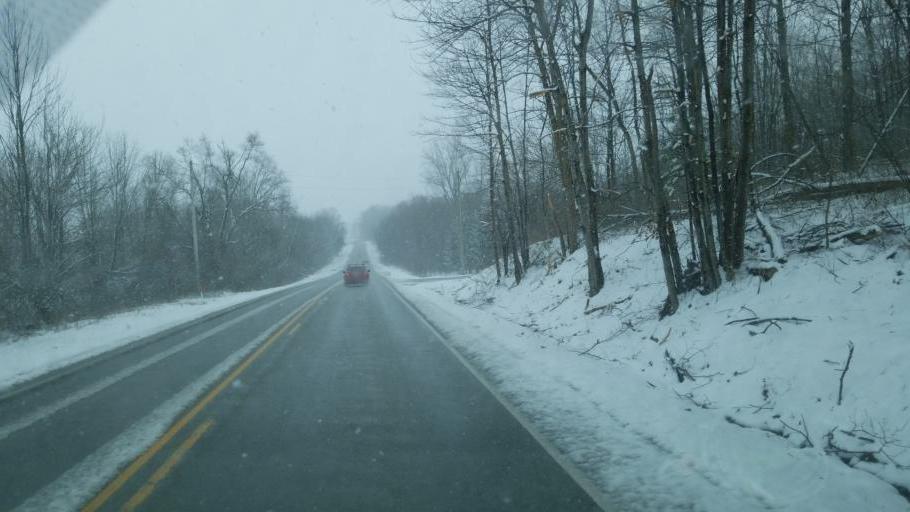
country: US
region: Indiana
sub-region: Wayne County
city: Hagerstown
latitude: 40.0107
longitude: -85.1676
